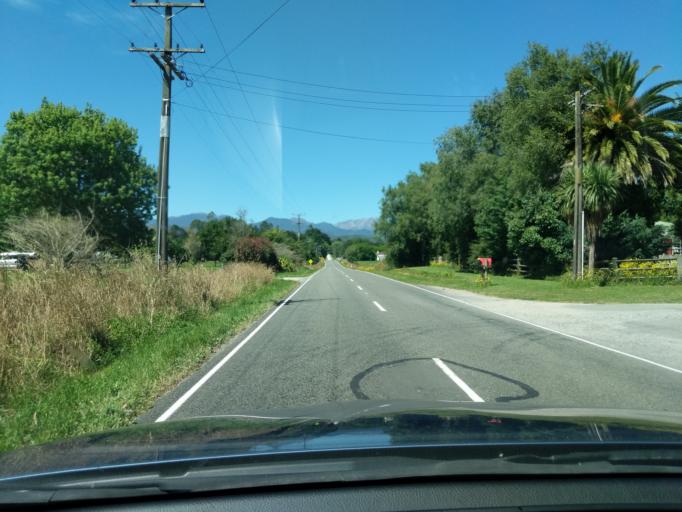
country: NZ
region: Tasman
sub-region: Tasman District
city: Takaka
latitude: -40.7257
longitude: 172.6378
